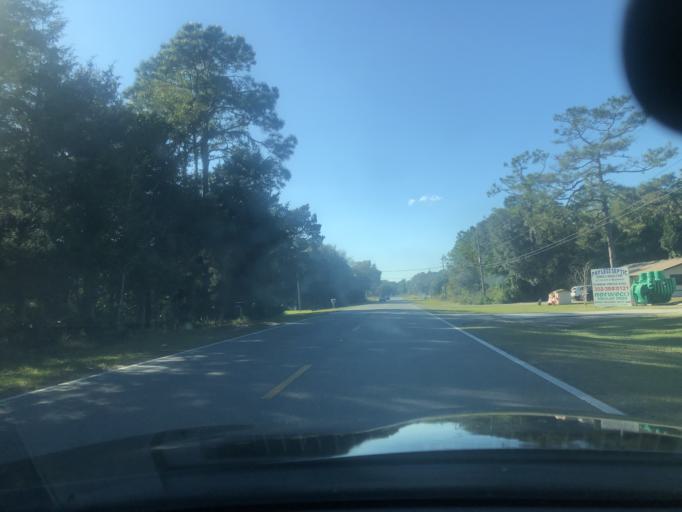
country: US
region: Florida
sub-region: Citrus County
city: Homosassa Springs
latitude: 28.8184
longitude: -82.5510
